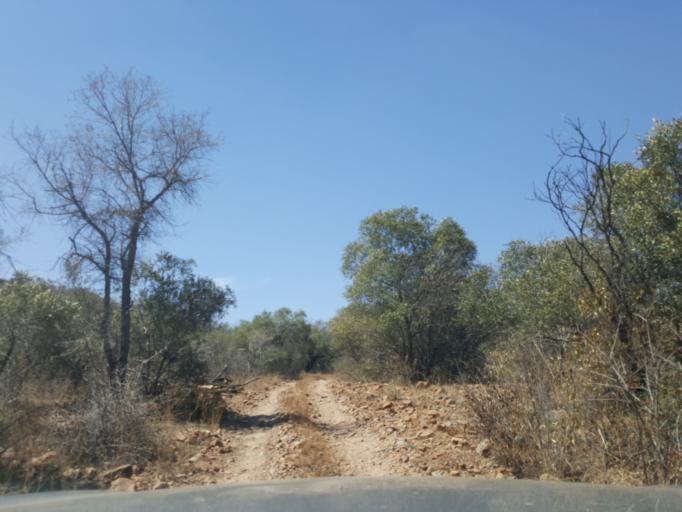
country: BW
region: South East
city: Lobatse
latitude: -25.1588
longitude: 25.6821
